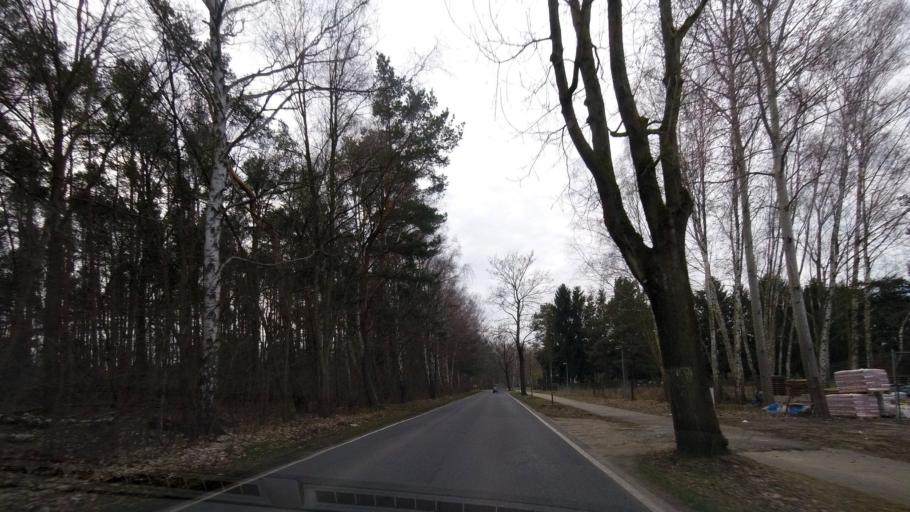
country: DE
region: Berlin
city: Schmockwitz
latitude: 52.3664
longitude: 13.6996
